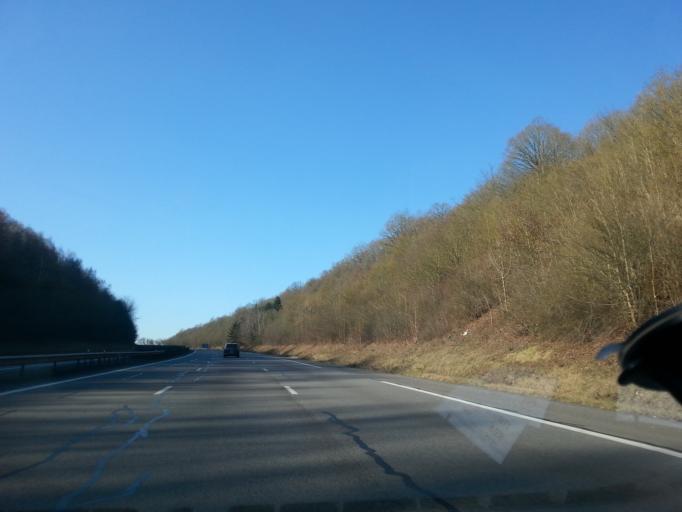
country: FR
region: Ile-de-France
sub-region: Departement des Yvelines
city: Bonnieres-sur-Seine
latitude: 49.0182
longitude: 1.5826
